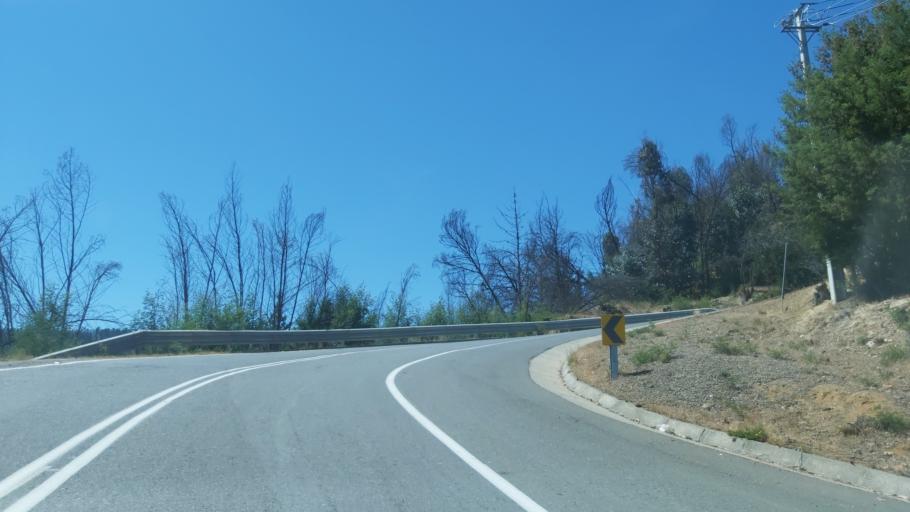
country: CL
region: Maule
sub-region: Provincia de Talca
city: Constitucion
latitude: -34.9093
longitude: -71.9966
